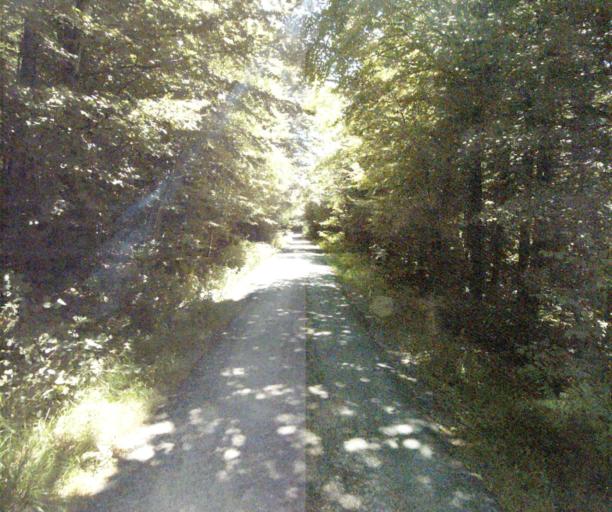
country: FR
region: Languedoc-Roussillon
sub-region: Departement de l'Aude
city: Cuxac-Cabardes
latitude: 43.4051
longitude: 2.2034
